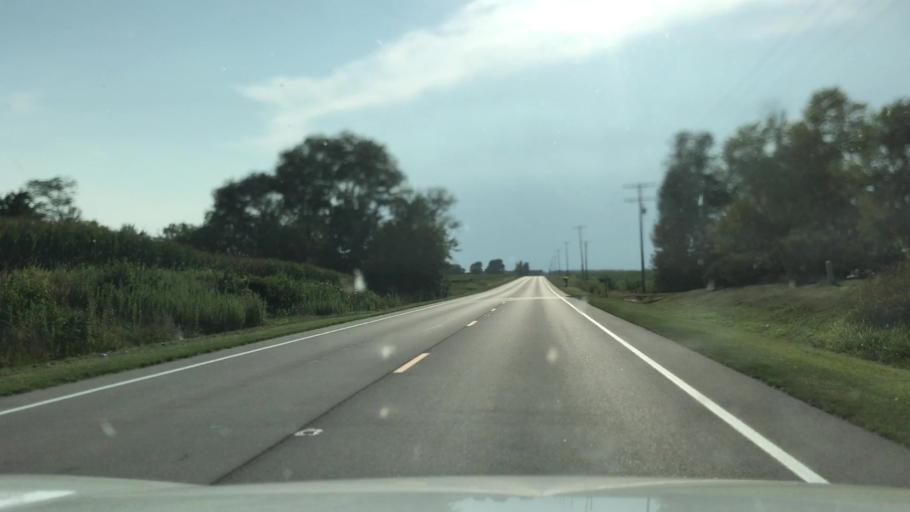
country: US
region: Illinois
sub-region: Washington County
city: Nashville
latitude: 38.4417
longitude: -89.3780
